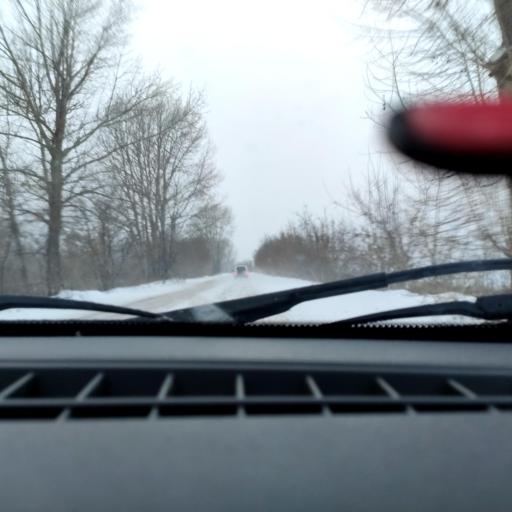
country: RU
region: Bashkortostan
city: Blagoveshchensk
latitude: 54.9111
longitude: 56.0031
